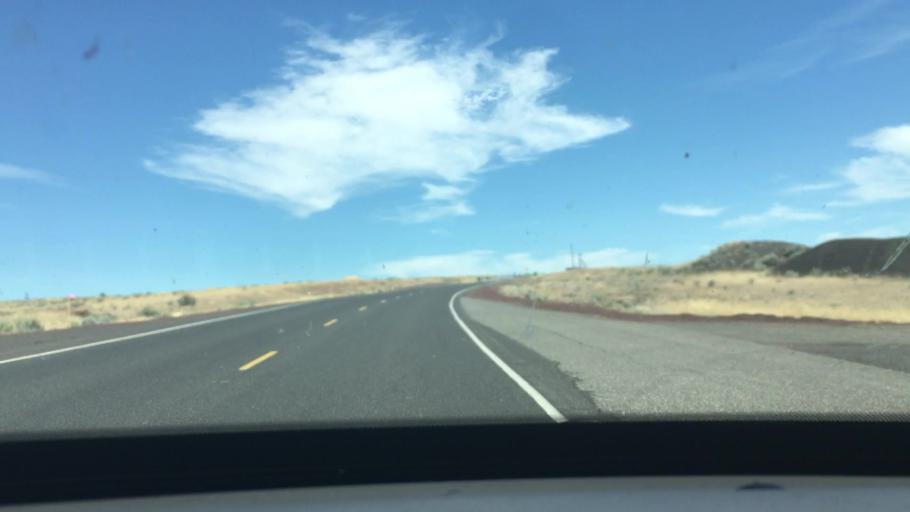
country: US
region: Oregon
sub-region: Jefferson County
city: Madras
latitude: 44.9911
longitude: -120.8523
